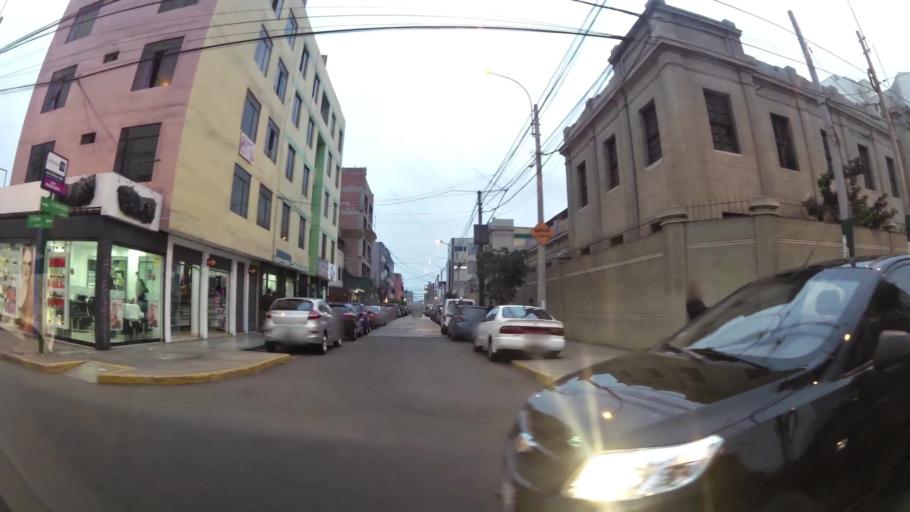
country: PE
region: Lima
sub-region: Lima
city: San Isidro
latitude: -12.0914
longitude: -77.0706
